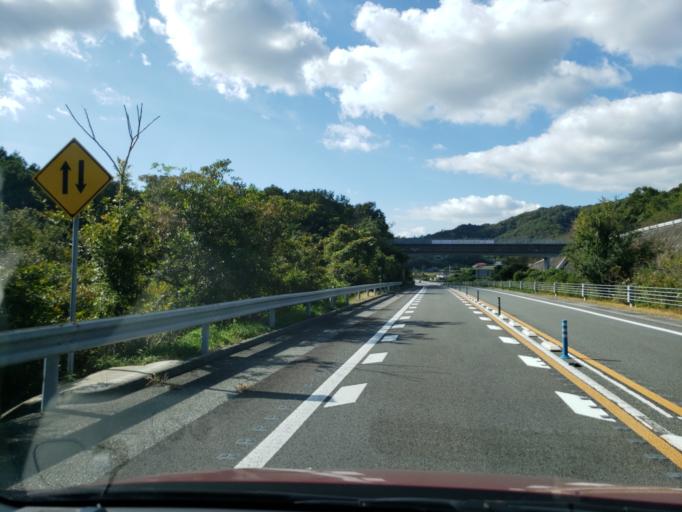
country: JP
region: Tokushima
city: Ishii
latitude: 34.1369
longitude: 134.3990
